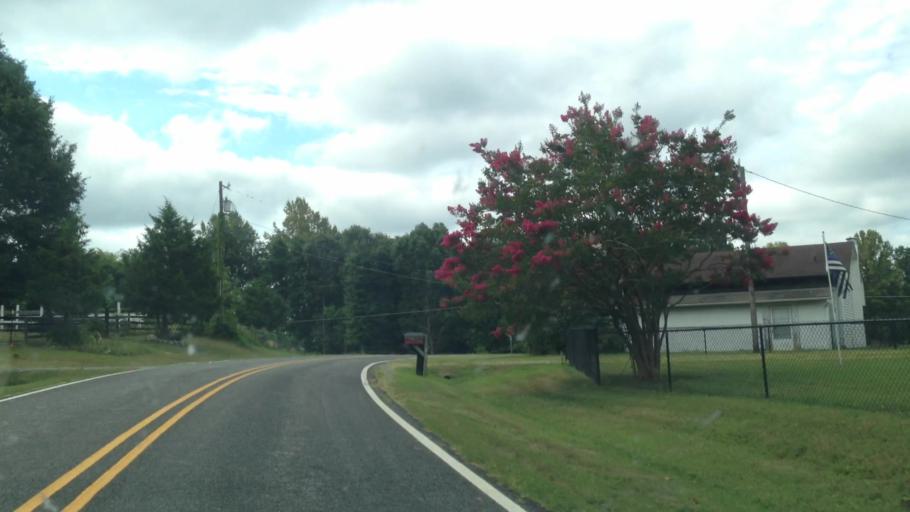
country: US
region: North Carolina
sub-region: Rockingham County
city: Mayodan
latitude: 36.4258
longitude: -80.0855
